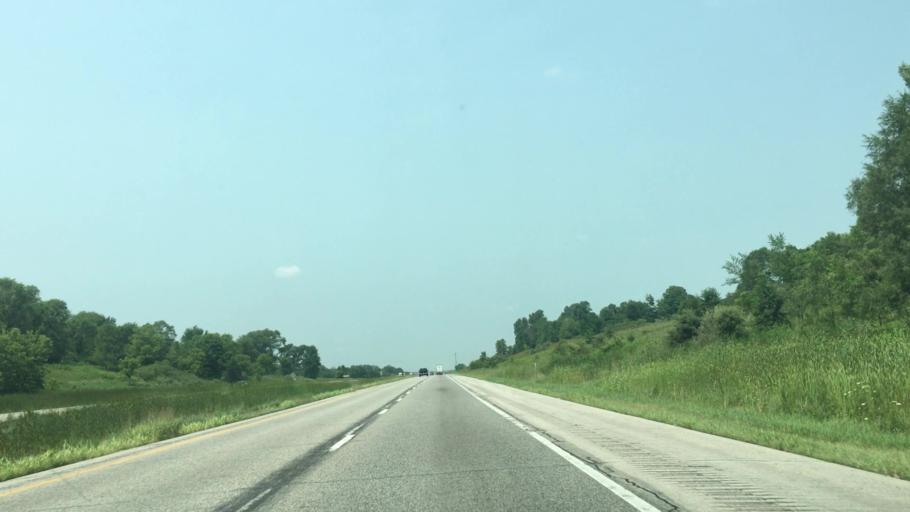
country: US
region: Iowa
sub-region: Benton County
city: Urbana
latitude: 42.2181
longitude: -91.8492
